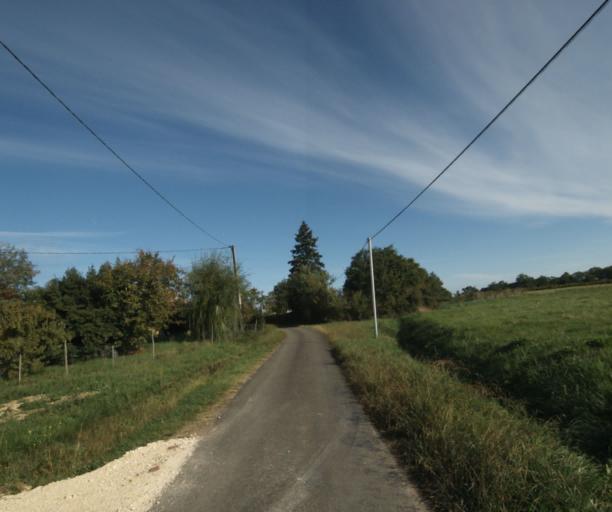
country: FR
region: Midi-Pyrenees
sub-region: Departement du Gers
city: Eauze
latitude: 43.8903
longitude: 0.1326
